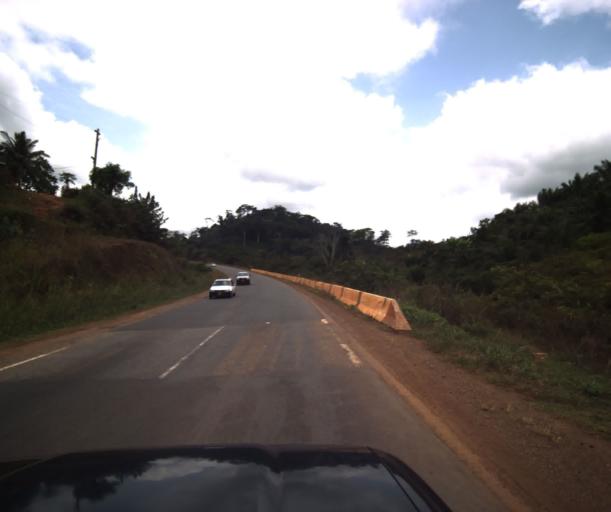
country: CM
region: Centre
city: Mbankomo
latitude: 3.7714
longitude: 11.0886
